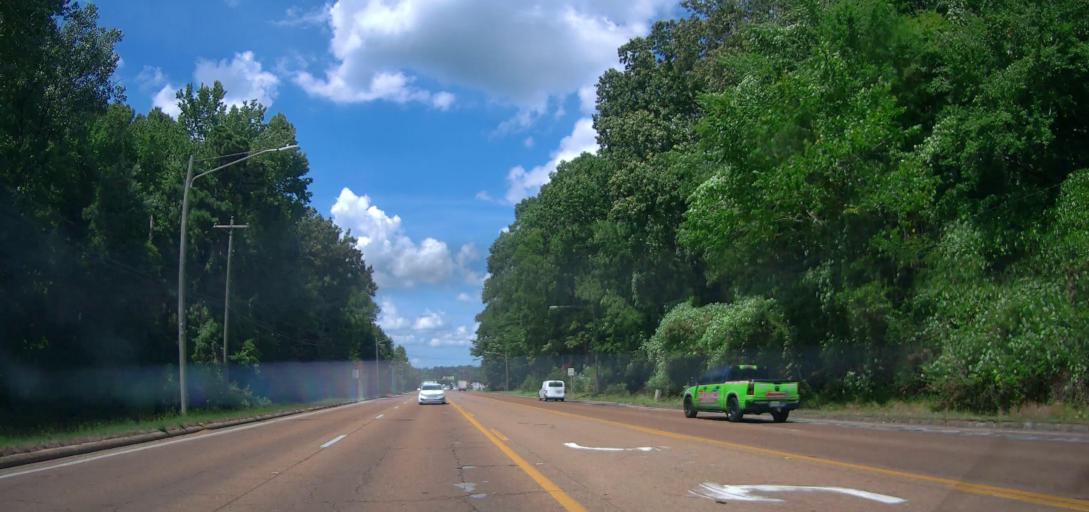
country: US
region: Mississippi
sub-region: Lowndes County
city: Columbus
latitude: 33.5430
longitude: -88.4367
